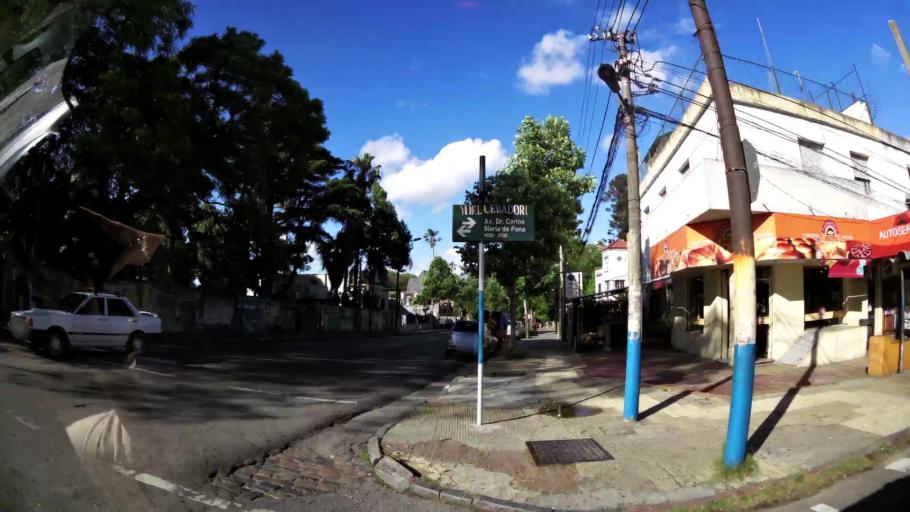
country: UY
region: Montevideo
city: Montevideo
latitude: -34.8532
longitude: -56.2084
